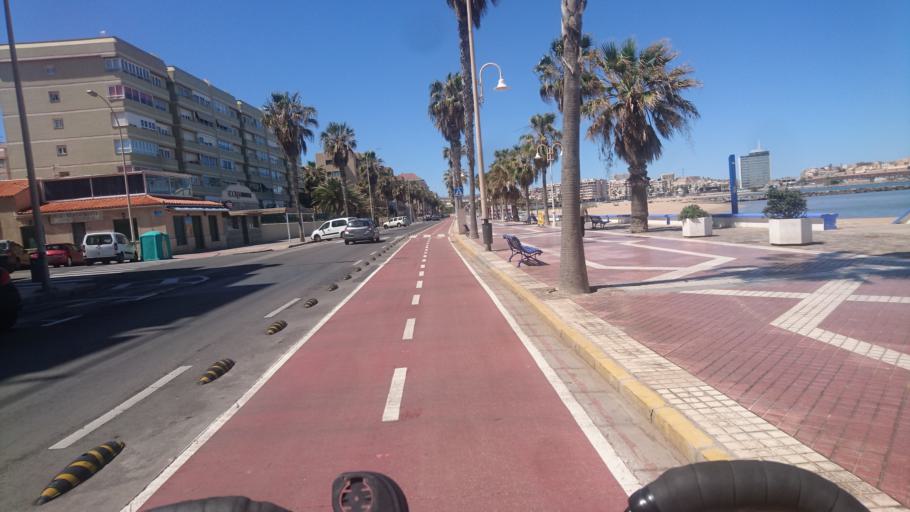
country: ES
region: Melilla
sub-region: Melilla
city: Melilla
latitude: 35.2810
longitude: -2.9372
